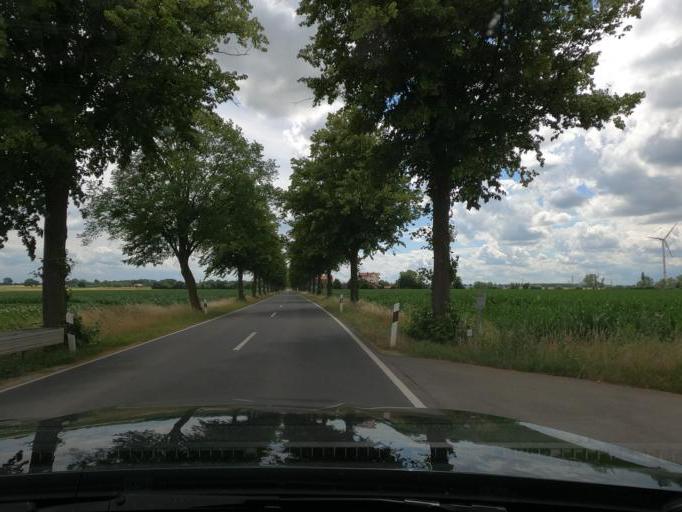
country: DE
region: Lower Saxony
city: Algermissen
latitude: 52.2608
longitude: 10.0147
